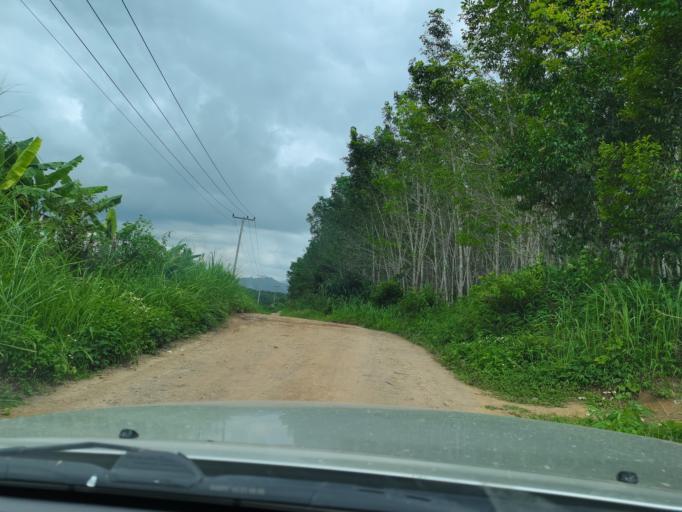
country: LA
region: Loungnamtha
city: Muang Long
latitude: 20.6984
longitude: 101.0368
